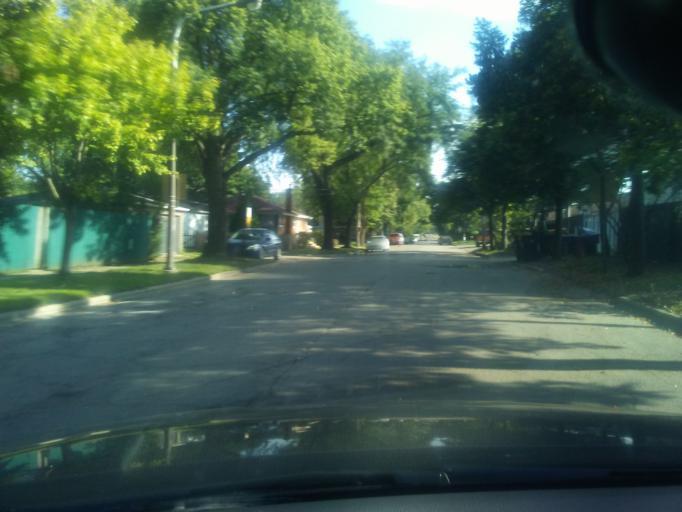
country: US
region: Illinois
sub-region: Cook County
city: Evanston
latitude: 42.0300
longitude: -87.7041
